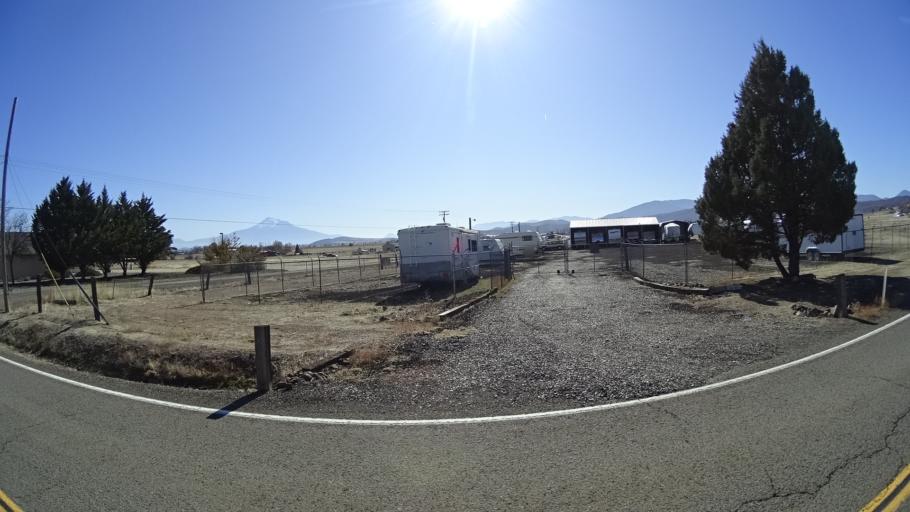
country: US
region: California
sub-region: Siskiyou County
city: Yreka
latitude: 41.7424
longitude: -122.5936
